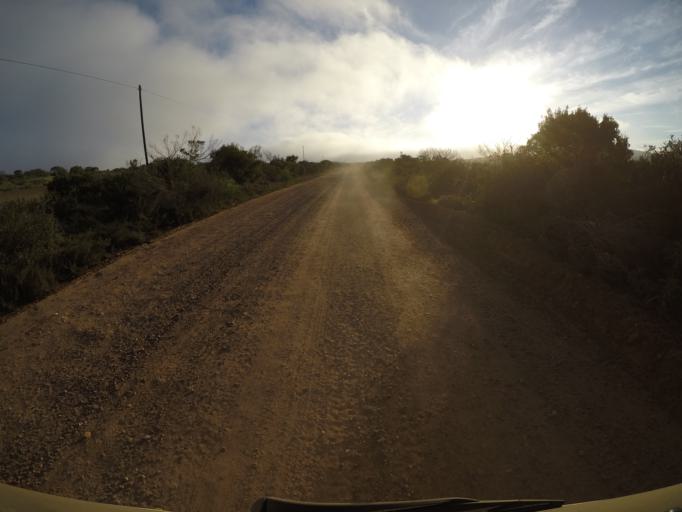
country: ZA
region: Western Cape
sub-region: Eden District Municipality
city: Mossel Bay
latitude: -34.1442
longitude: 22.0213
